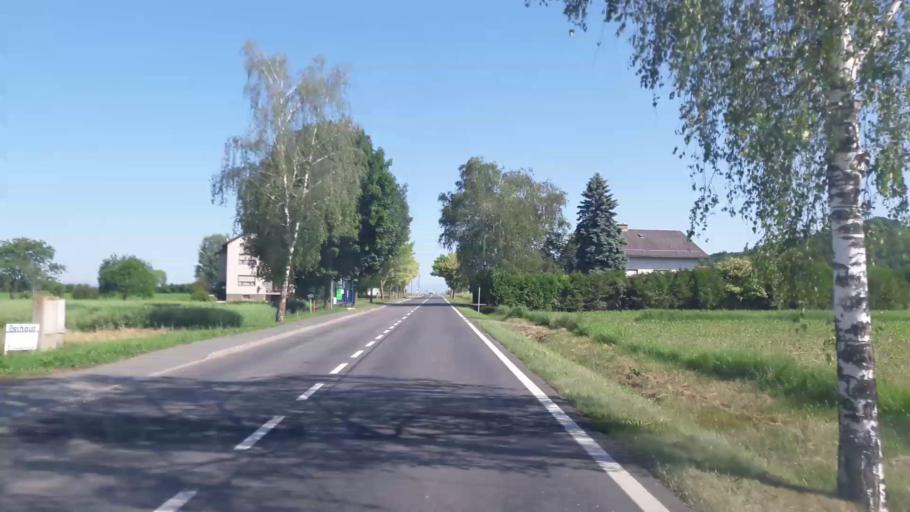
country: AT
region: Burgenland
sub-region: Politischer Bezirk Jennersdorf
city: Rudersdorf
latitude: 47.0569
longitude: 16.1180
